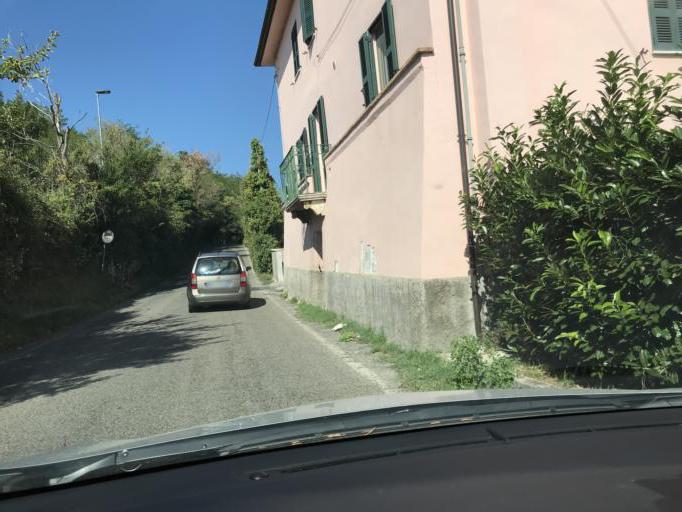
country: IT
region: Umbria
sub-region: Provincia di Perugia
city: Perugia
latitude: 43.1095
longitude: 12.4206
